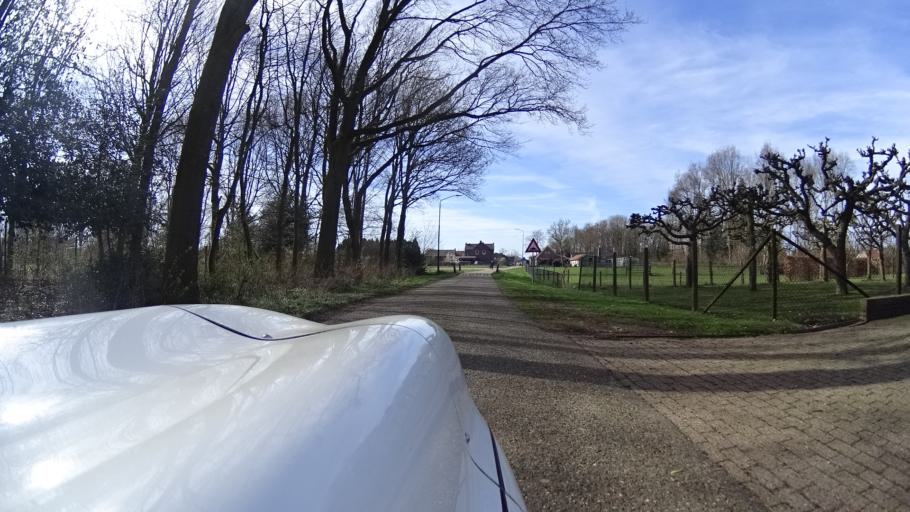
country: NL
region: Limburg
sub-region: Gemeente Gennep
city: Gennep
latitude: 51.7048
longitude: 5.9367
